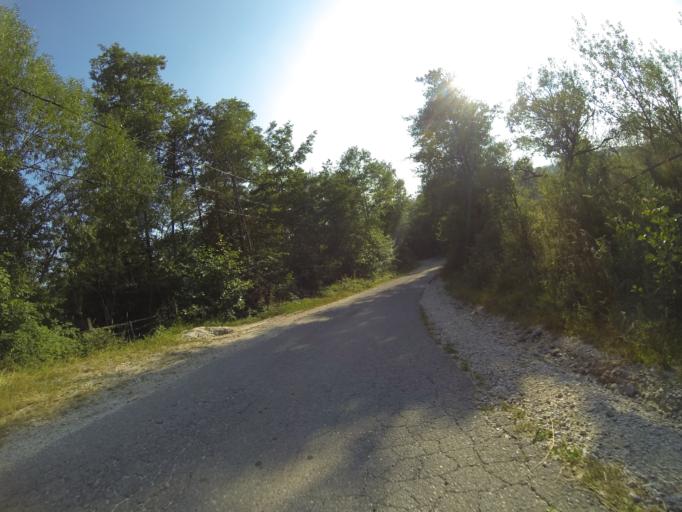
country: RO
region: Valcea
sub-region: Comuna Horezu
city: Horezu
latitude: 45.1737
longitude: 23.9875
